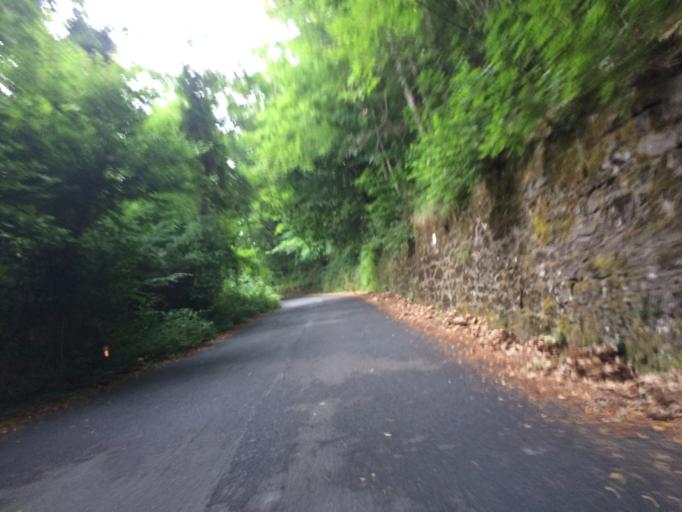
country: IT
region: Liguria
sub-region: Provincia di Imperia
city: Triora
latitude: 43.9858
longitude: 7.7600
